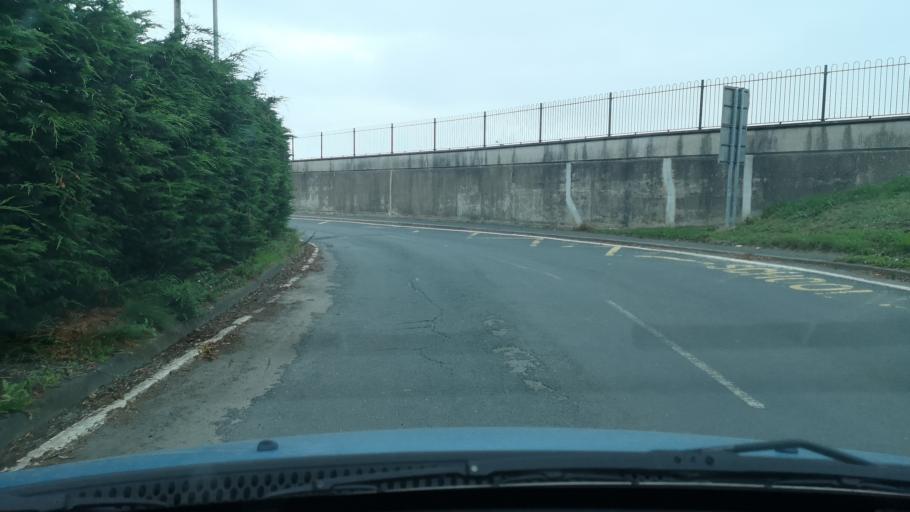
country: GB
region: England
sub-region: East Riding of Yorkshire
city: Laxton
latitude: 53.6956
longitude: -0.7839
